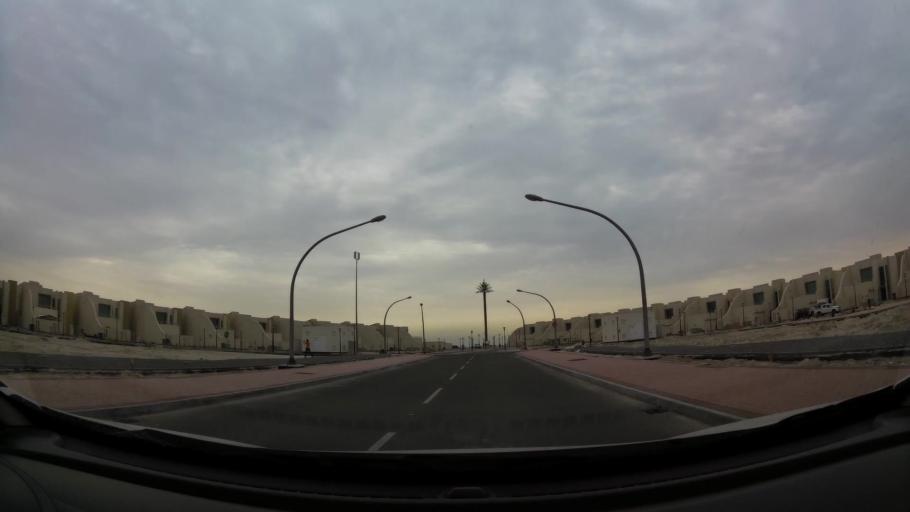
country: BH
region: Central Governorate
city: Dar Kulayb
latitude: 25.8288
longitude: 50.6109
